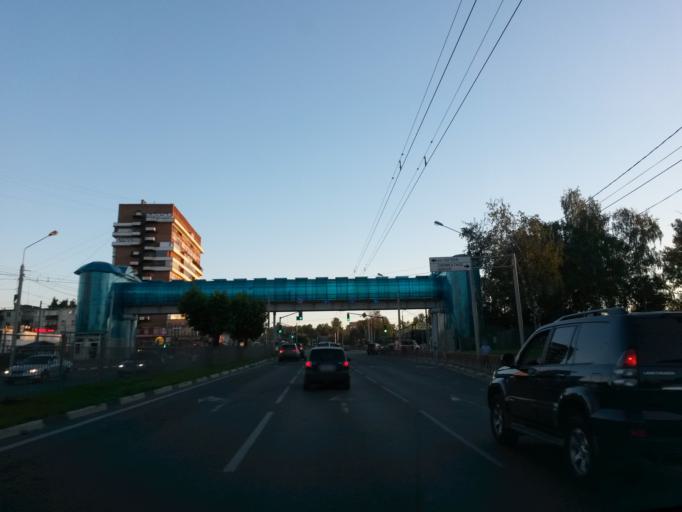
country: RU
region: Jaroslavl
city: Yaroslavl
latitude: 57.5937
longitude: 39.8648
